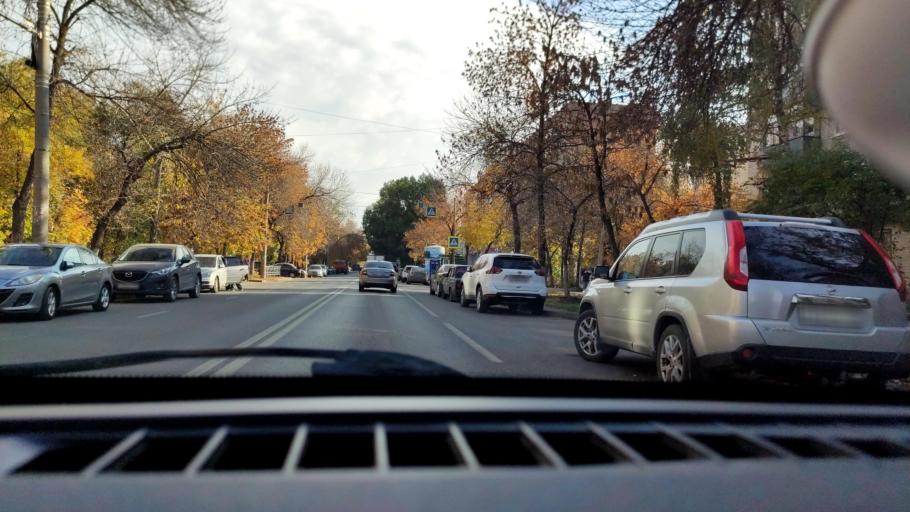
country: RU
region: Samara
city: Samara
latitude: 53.1963
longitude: 50.1655
